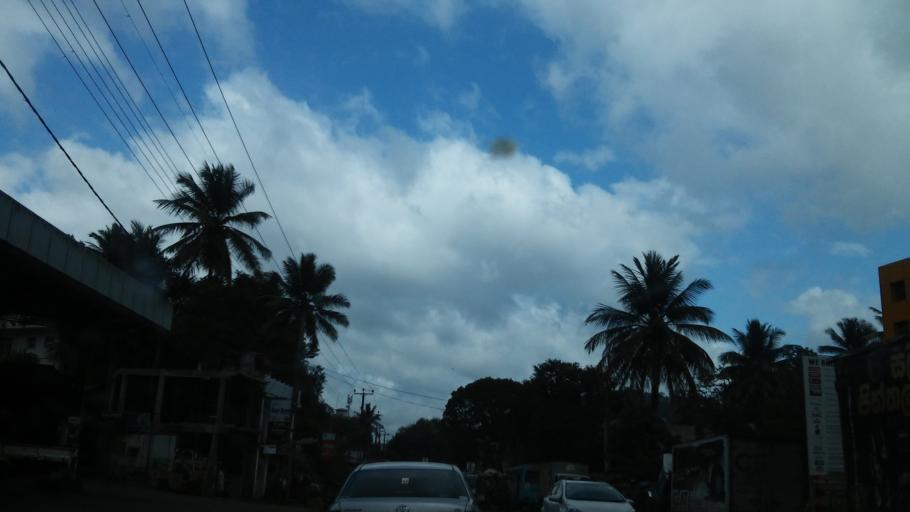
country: LK
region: Central
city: Kandy
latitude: 7.2836
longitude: 80.6257
